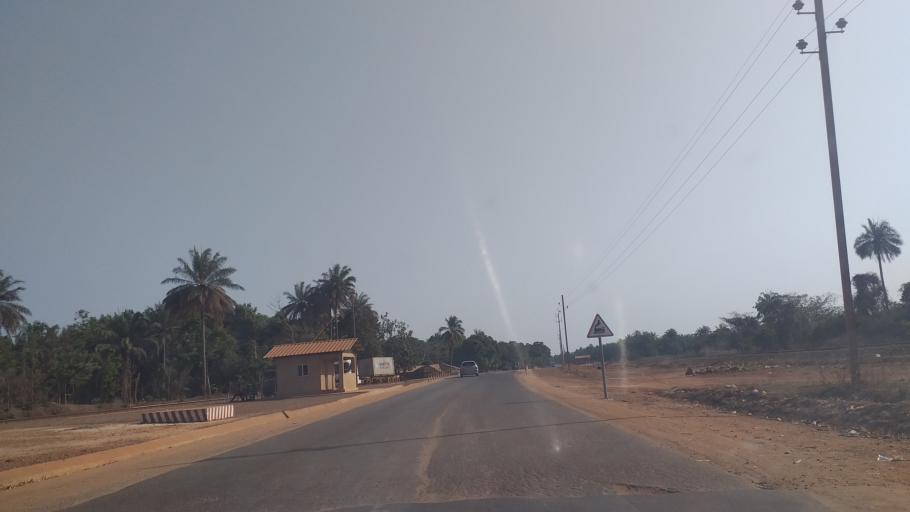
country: GN
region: Boke
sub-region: Boke Prefecture
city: Kamsar
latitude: 10.7377
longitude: -14.5151
